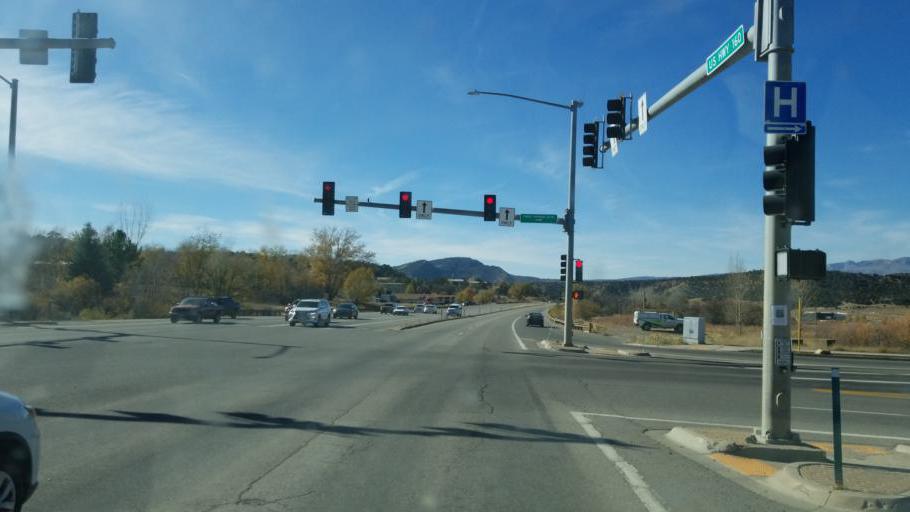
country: US
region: Colorado
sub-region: La Plata County
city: Durango
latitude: 37.2272
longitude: -107.8199
